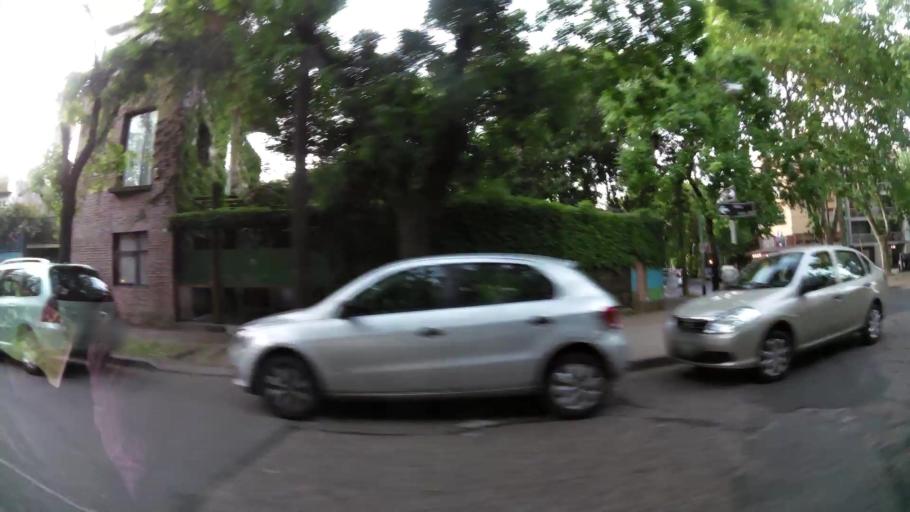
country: AR
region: Buenos Aires F.D.
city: Colegiales
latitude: -34.5502
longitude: -58.4824
